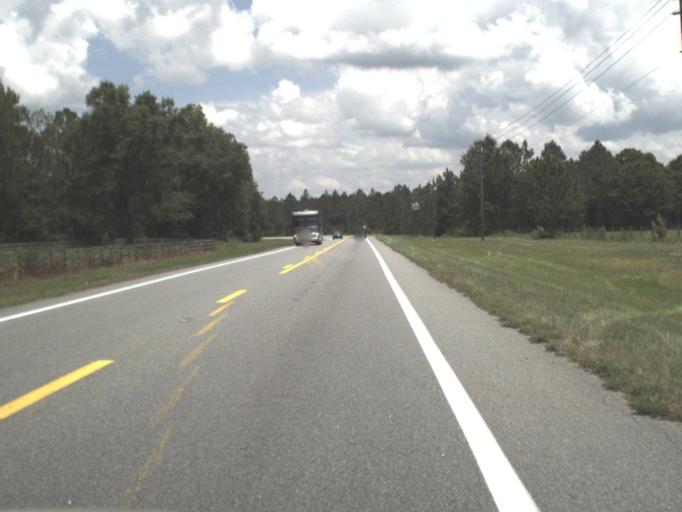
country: US
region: Florida
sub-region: Union County
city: Lake Butler
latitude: 30.0435
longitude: -82.2845
